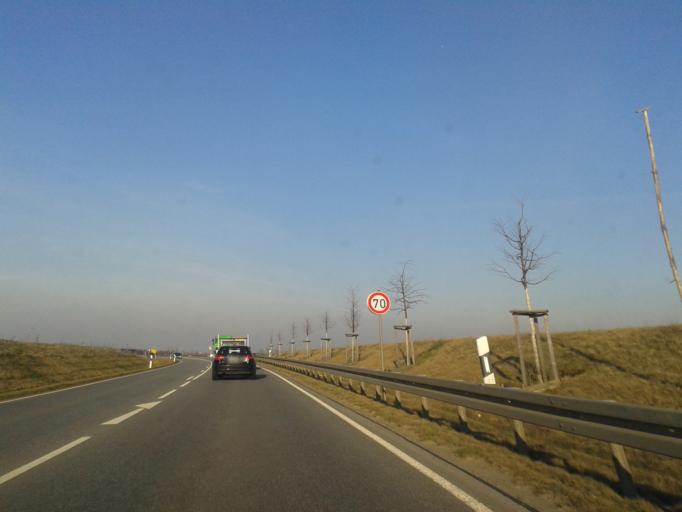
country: DE
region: Saxony
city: Wilsdruff
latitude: 51.0351
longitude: 13.5737
